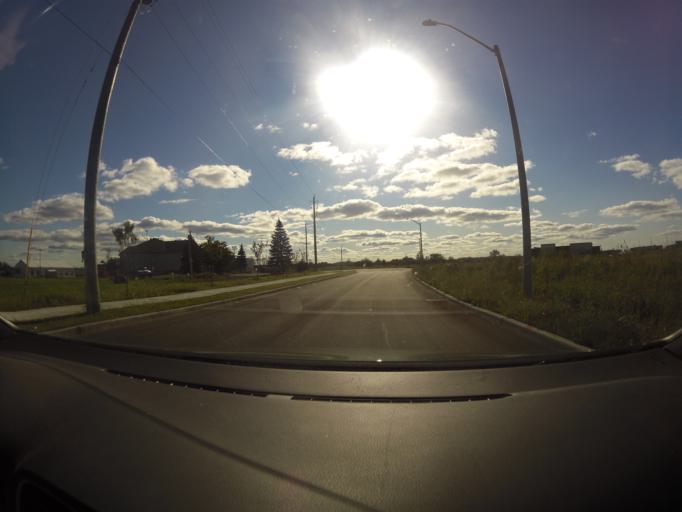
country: CA
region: Ontario
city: Bells Corners
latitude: 45.3043
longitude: -75.9190
